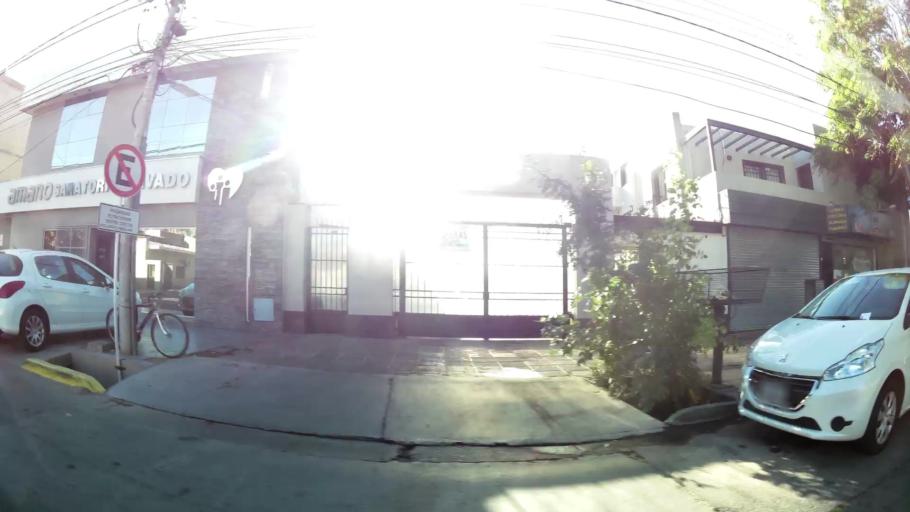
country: AR
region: Mendoza
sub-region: Departamento de Godoy Cruz
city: Godoy Cruz
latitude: -32.9229
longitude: -68.8499
